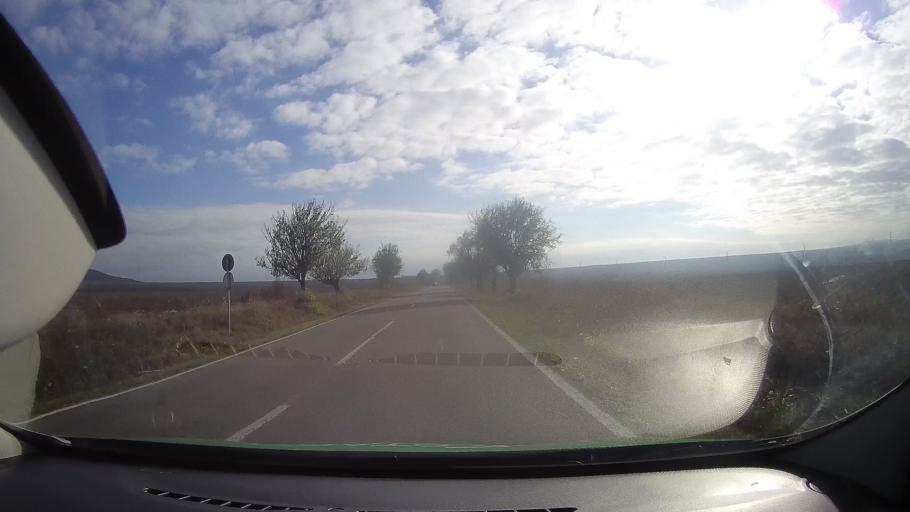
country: RO
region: Tulcea
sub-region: Comuna Bestepe
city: Bestepe
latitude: 45.0810
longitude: 29.0337
